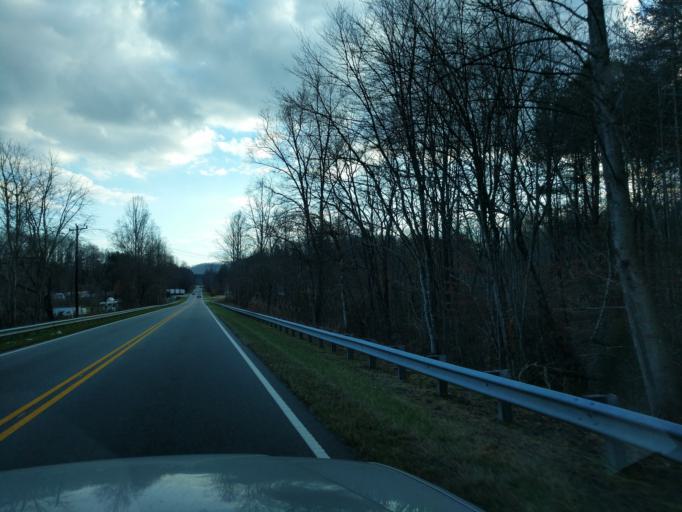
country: US
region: North Carolina
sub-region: McDowell County
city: West Marion
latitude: 35.6004
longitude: -81.9842
